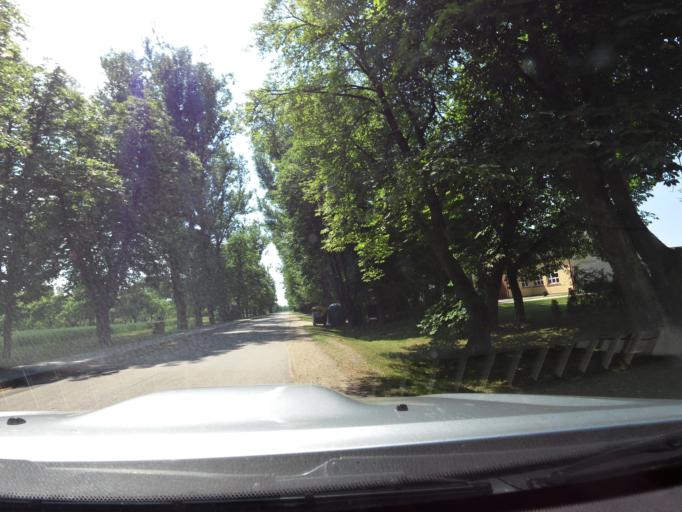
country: LT
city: Vilkaviskis
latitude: 54.6383
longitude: 22.9781
